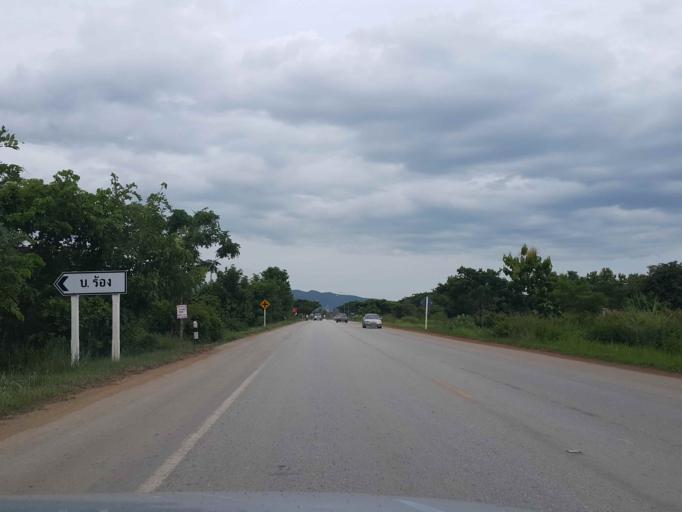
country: TH
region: Lampang
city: Lampang
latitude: 18.2585
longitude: 99.4769
